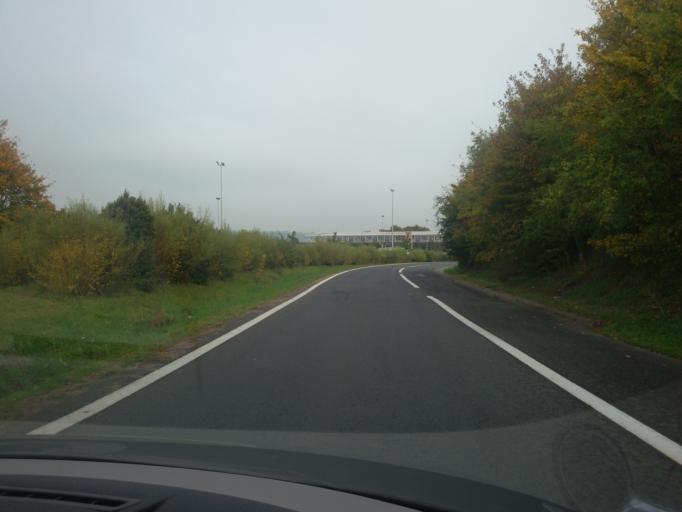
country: FR
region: Lower Normandy
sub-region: Departement du Calvados
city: Dozule
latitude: 49.2281
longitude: -0.0787
